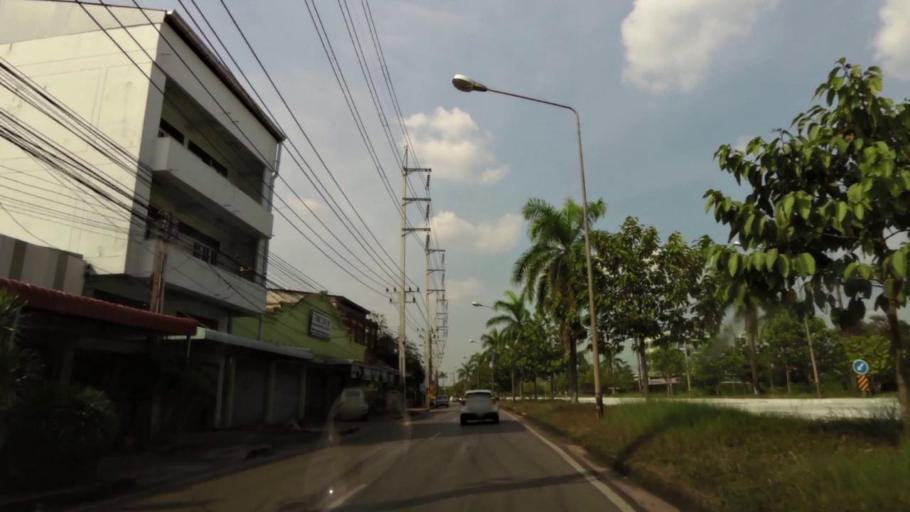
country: TH
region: Rayong
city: Klaeng
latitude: 12.7880
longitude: 101.6491
